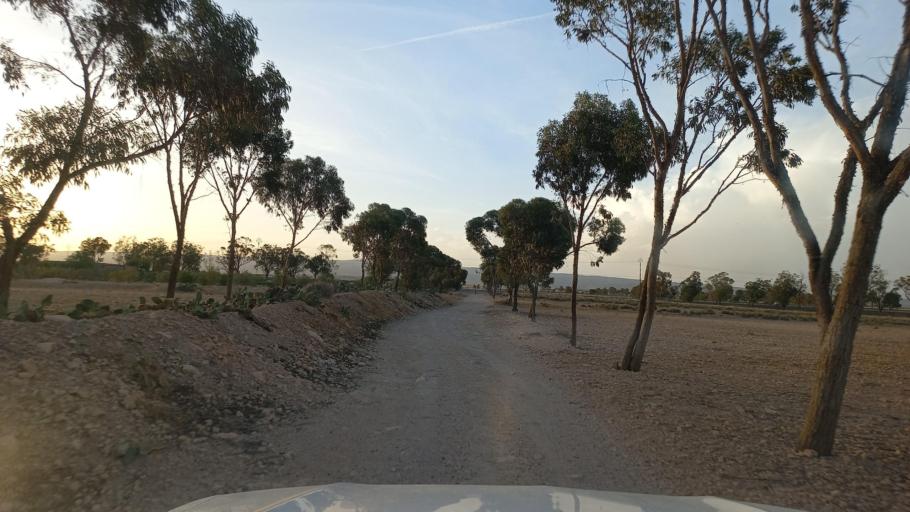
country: TN
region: Al Qasrayn
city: Kasserine
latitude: 35.2413
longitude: 8.9931
